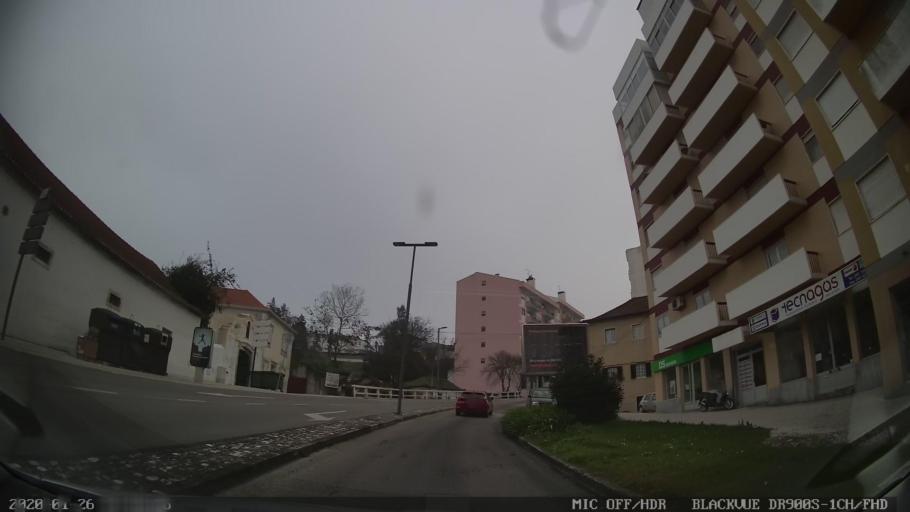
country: PT
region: Santarem
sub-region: Santarem
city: Santarem
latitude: 39.2418
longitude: -8.6880
